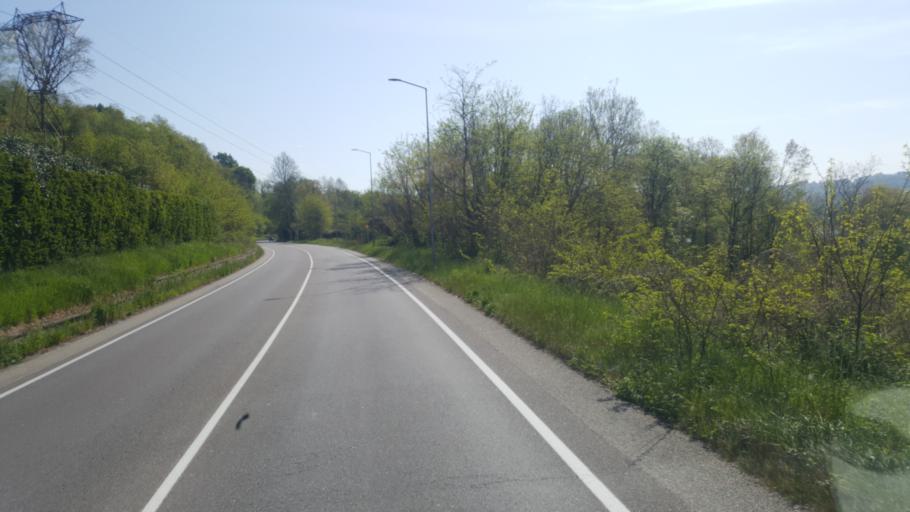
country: IT
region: Lombardy
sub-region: Provincia di Varese
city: Casciago
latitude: 45.8060
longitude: 8.7899
